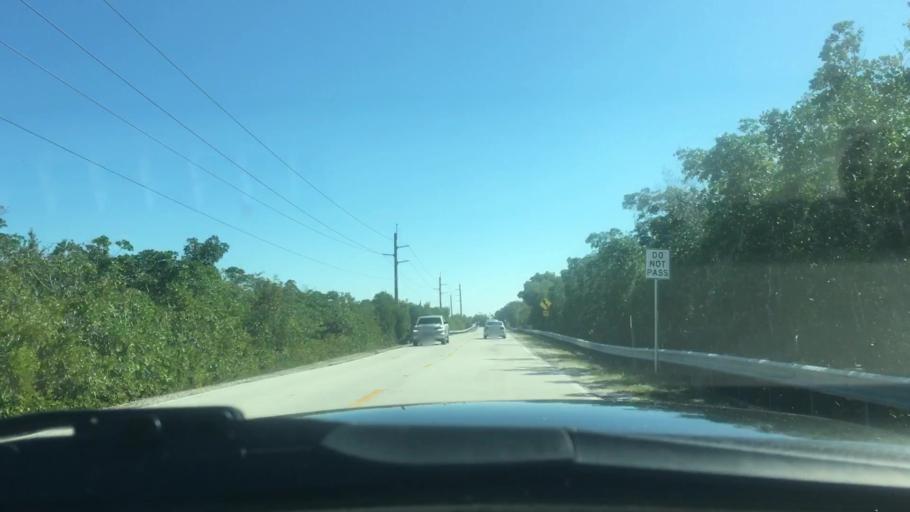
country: US
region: Florida
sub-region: Monroe County
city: North Key Largo
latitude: 25.2802
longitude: -80.3458
